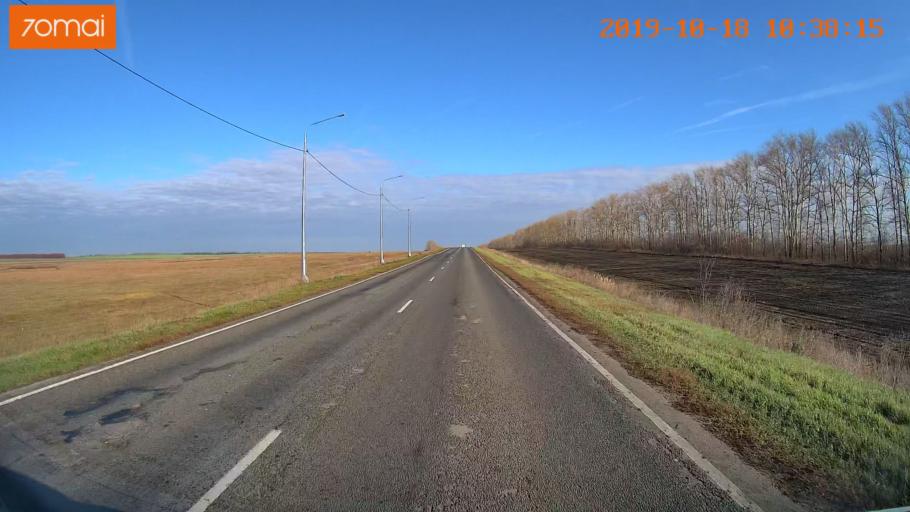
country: RU
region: Tula
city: Kurkino
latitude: 53.5705
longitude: 38.6394
